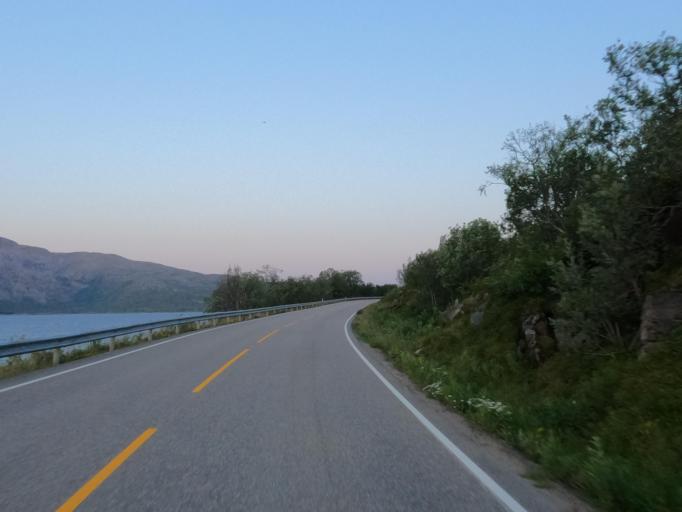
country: NO
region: Nordland
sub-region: Lodingen
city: Lodingen
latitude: 68.4987
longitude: 16.0956
